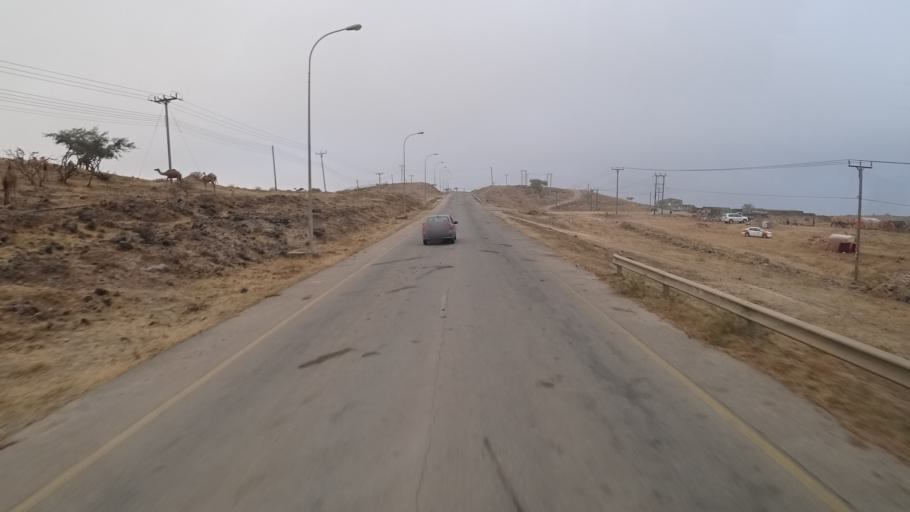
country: OM
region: Zufar
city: Salalah
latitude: 17.1269
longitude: 53.9763
